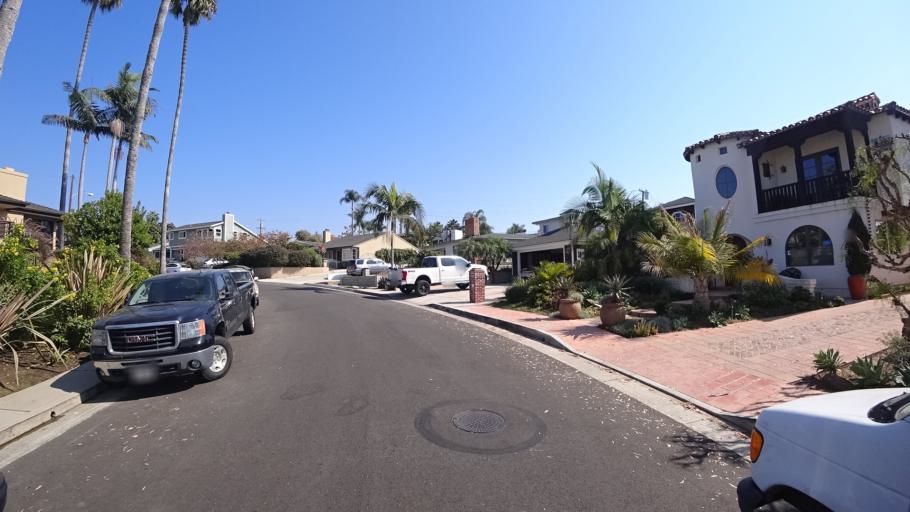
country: US
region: California
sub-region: Orange County
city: San Clemente
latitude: 33.4148
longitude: -117.6104
